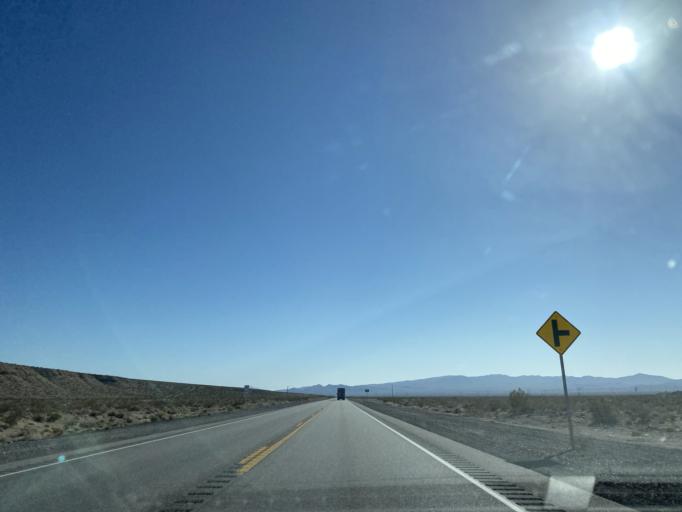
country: US
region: Nevada
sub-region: Nye County
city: Beatty
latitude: 36.8713
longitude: -116.7550
